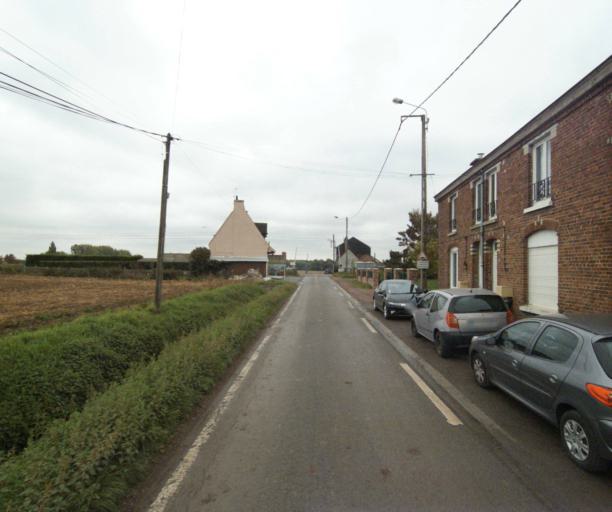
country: FR
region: Nord-Pas-de-Calais
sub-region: Departement du Nord
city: Santes
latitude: 50.5875
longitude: 2.9541
